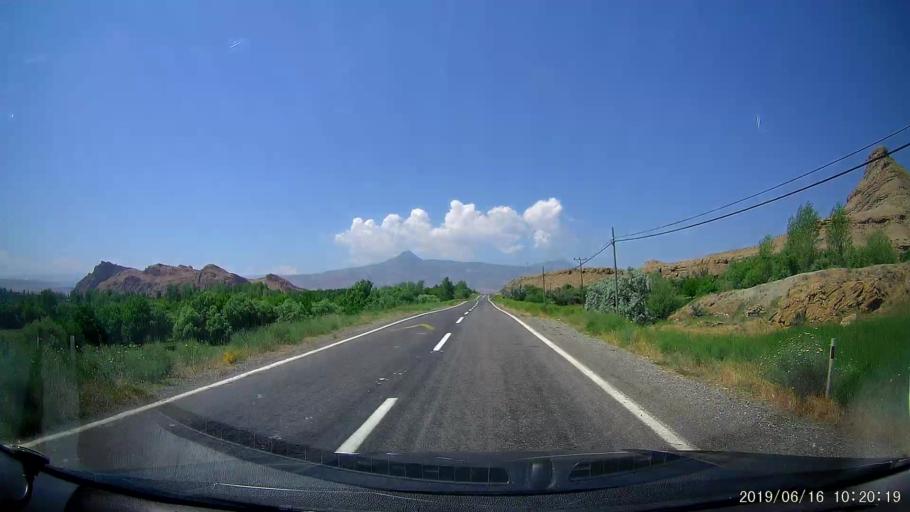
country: TR
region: Igdir
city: Tuzluca
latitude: 40.1488
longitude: 43.6489
